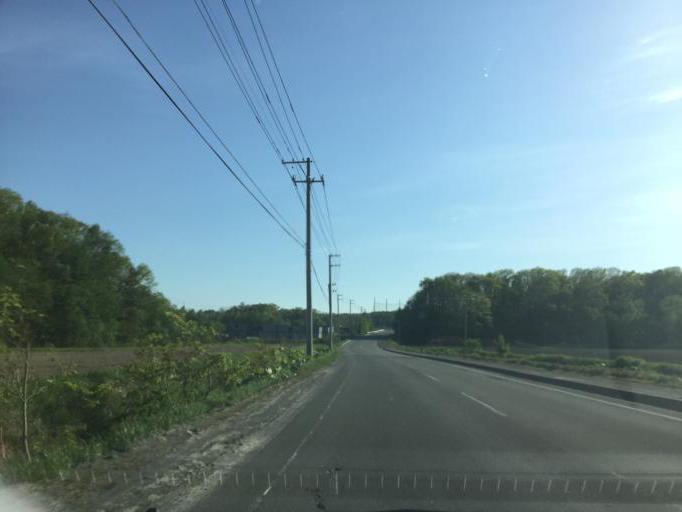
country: JP
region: Hokkaido
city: Kitahiroshima
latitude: 43.0032
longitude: 141.5488
